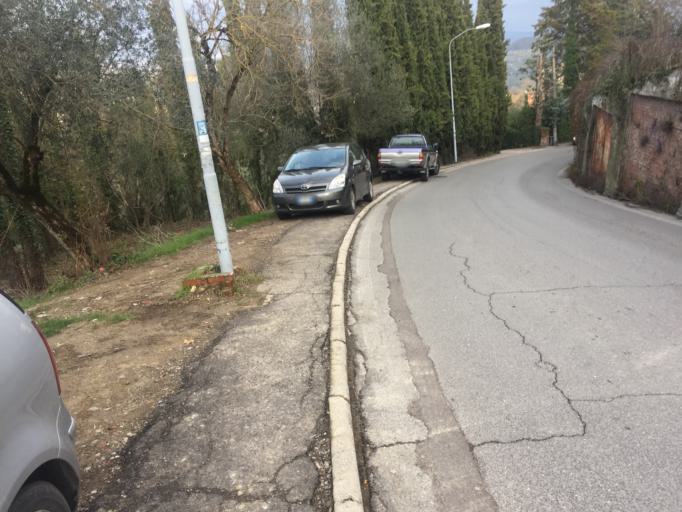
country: IT
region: Umbria
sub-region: Provincia di Perugia
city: Perugia
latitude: 43.1162
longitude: 12.3957
